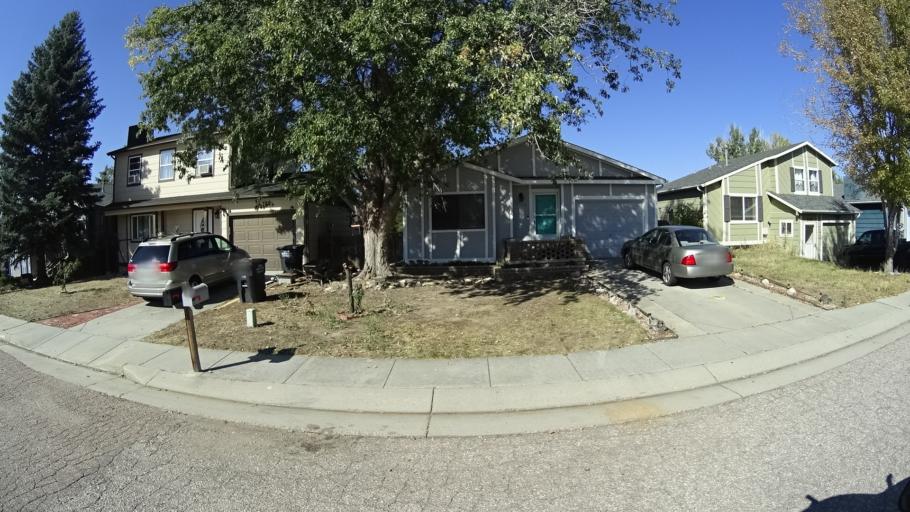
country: US
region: Colorado
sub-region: El Paso County
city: Cimarron Hills
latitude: 38.8708
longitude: -104.7085
